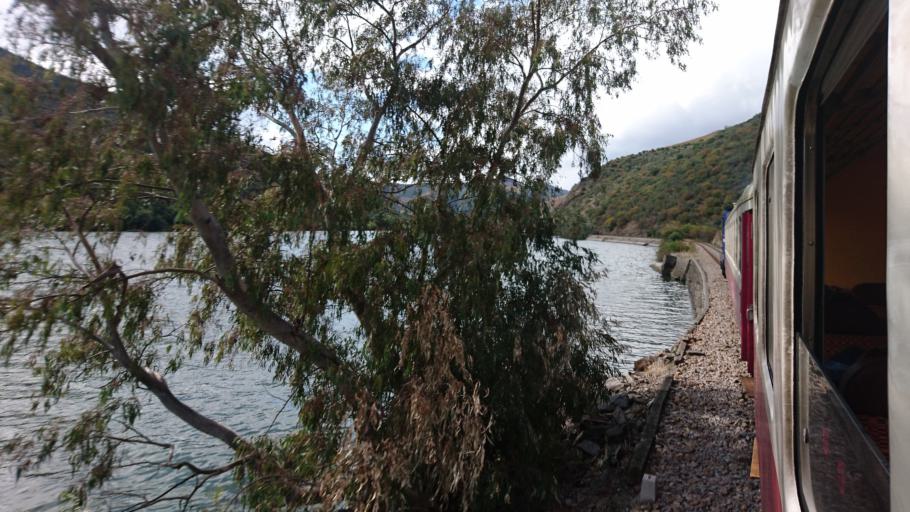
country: PT
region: Viseu
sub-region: Armamar
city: Armamar
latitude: 41.1632
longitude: -7.6645
